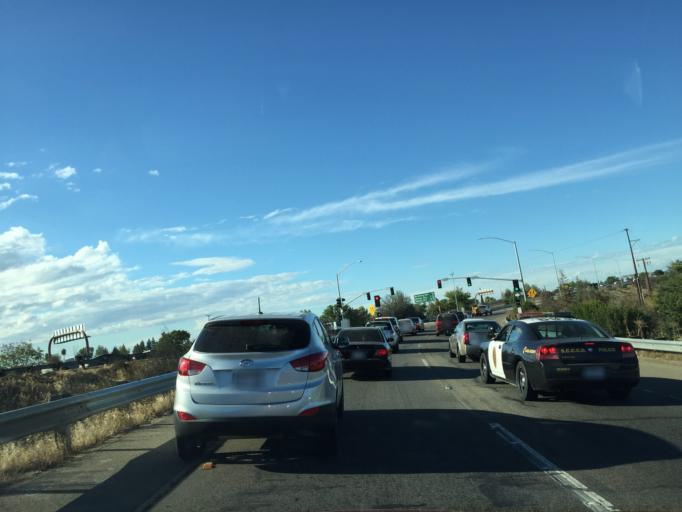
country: US
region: California
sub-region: Fresno County
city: Fresno
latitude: 36.7562
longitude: -119.7747
